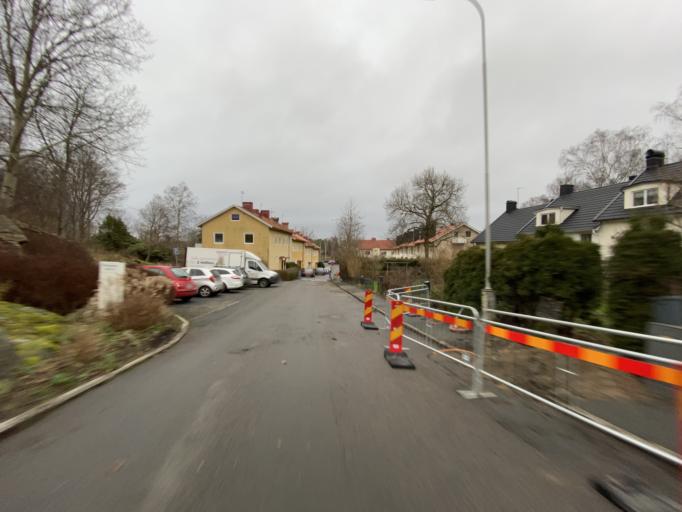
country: SE
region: Vaestra Goetaland
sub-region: Goteborg
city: Eriksbo
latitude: 57.7162
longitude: 12.0398
